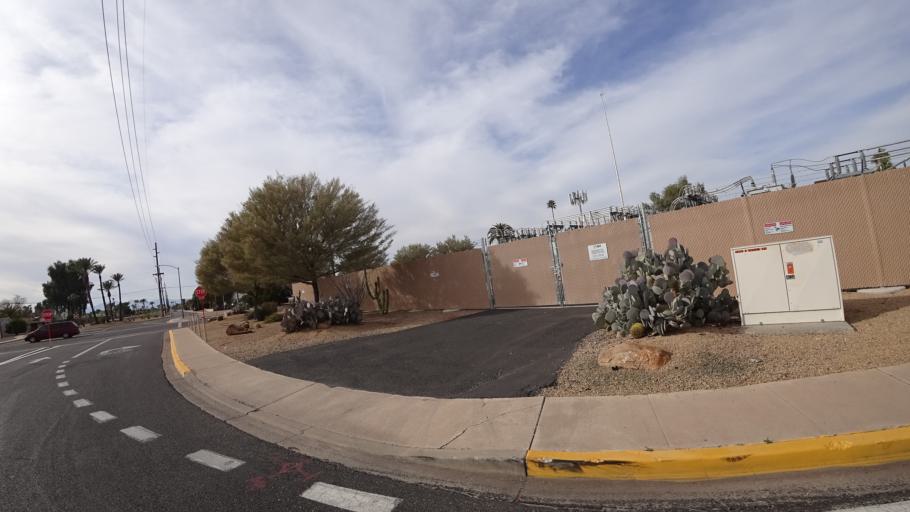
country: US
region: Arizona
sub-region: Maricopa County
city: Sun City
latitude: 33.5948
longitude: -112.2807
